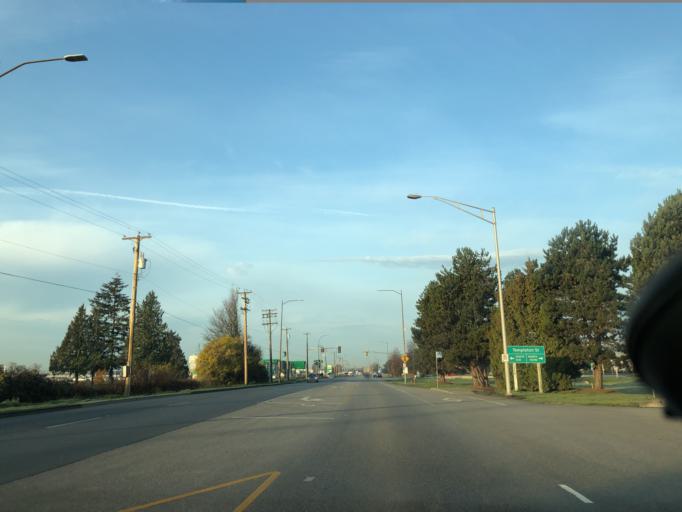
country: CA
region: British Columbia
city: Richmond
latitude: 49.1922
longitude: -123.1484
